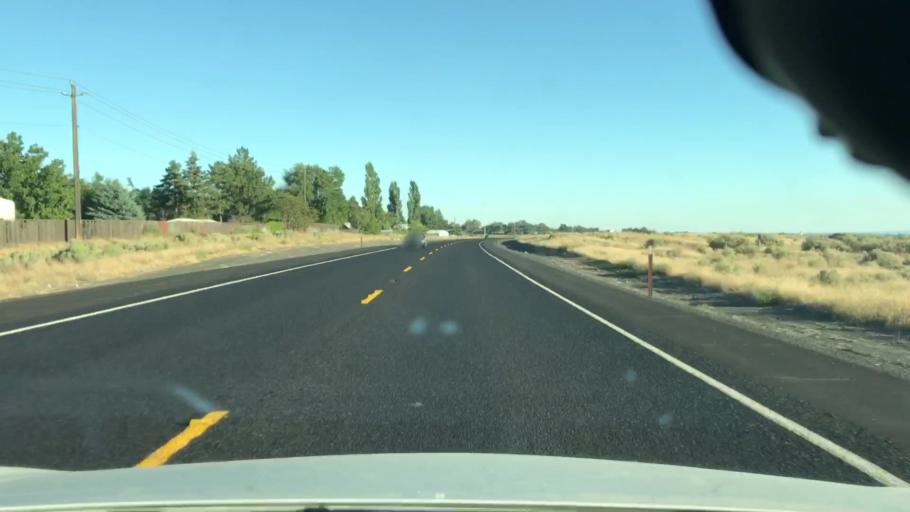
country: US
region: Washington
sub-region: Grant County
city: Moses Lake North
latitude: 47.1788
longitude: -119.3336
